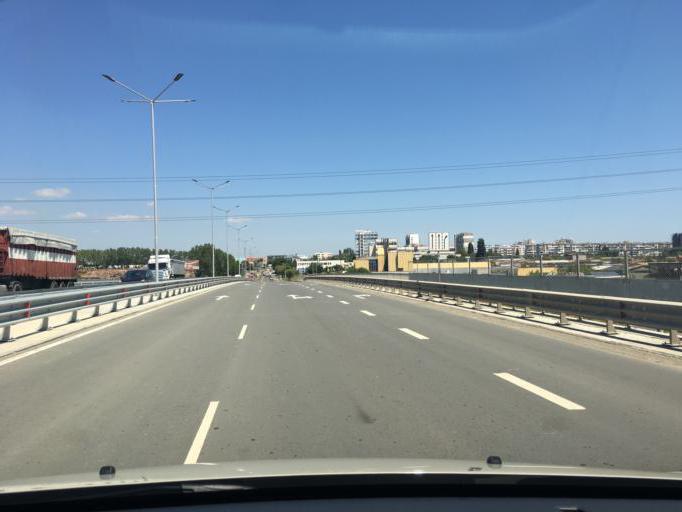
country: BG
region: Burgas
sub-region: Obshtina Burgas
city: Burgas
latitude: 42.5149
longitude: 27.4363
